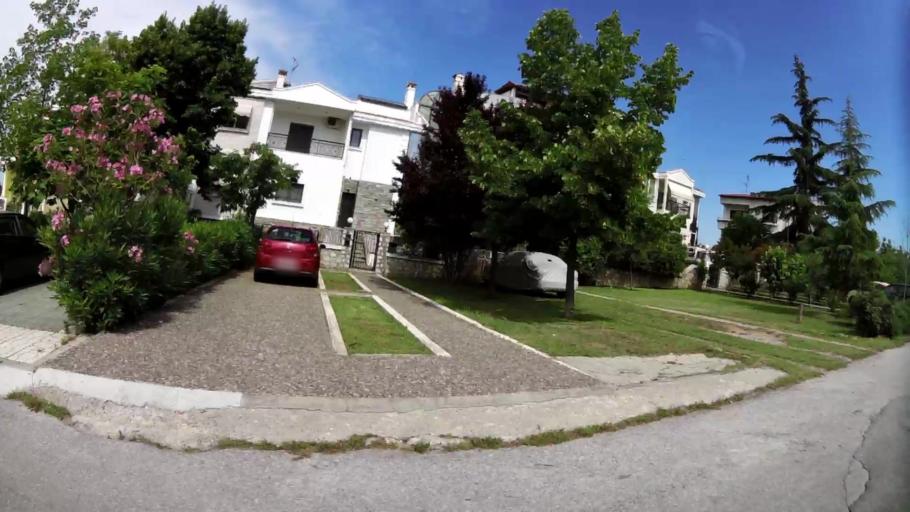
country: GR
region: Central Macedonia
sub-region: Nomos Thessalonikis
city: Panorama
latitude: 40.5818
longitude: 23.0074
